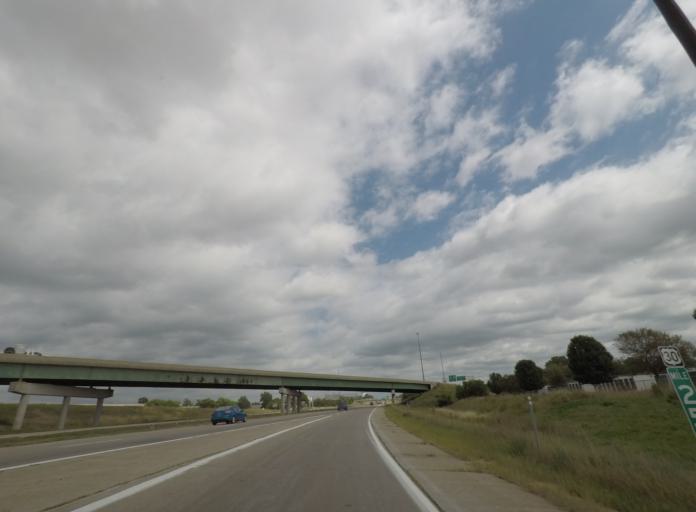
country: US
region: Iowa
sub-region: Linn County
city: Cedar Rapids
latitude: 41.9267
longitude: -91.6656
